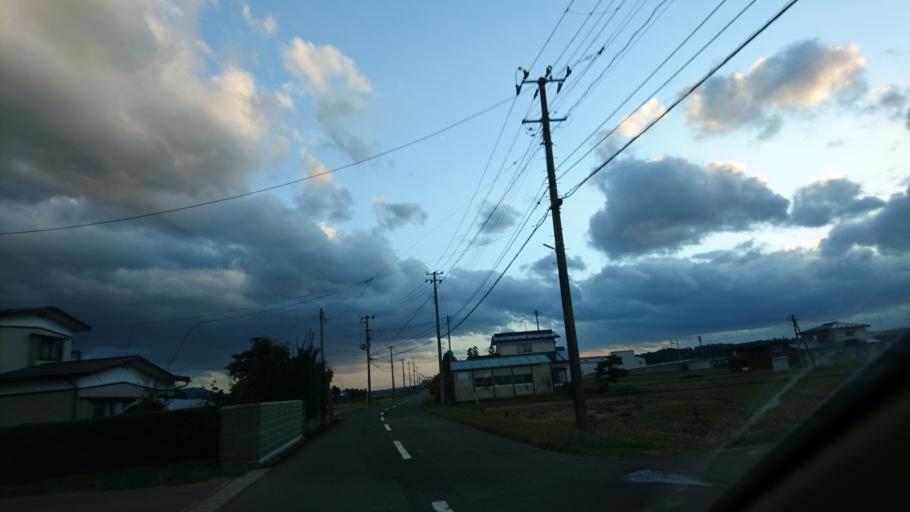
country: JP
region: Iwate
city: Mizusawa
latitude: 39.1014
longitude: 141.1472
